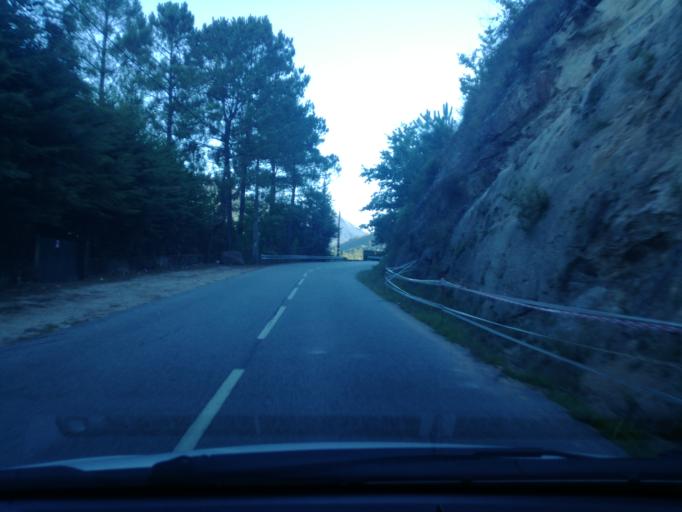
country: PT
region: Braga
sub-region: Vieira do Minho
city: Real
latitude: 41.6950
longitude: -8.1708
